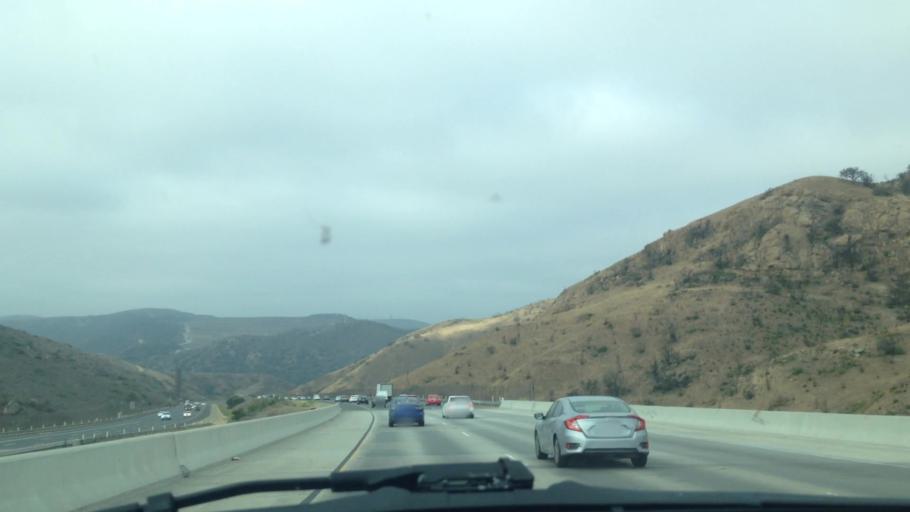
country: US
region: California
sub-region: Orange County
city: North Tustin
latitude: 33.8078
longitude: -117.7240
